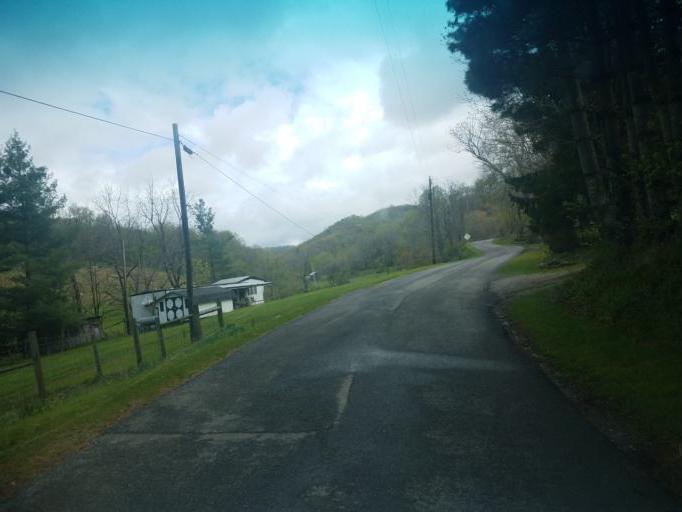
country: US
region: Virginia
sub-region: Smyth County
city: Atkins
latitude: 36.9778
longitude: -81.3960
